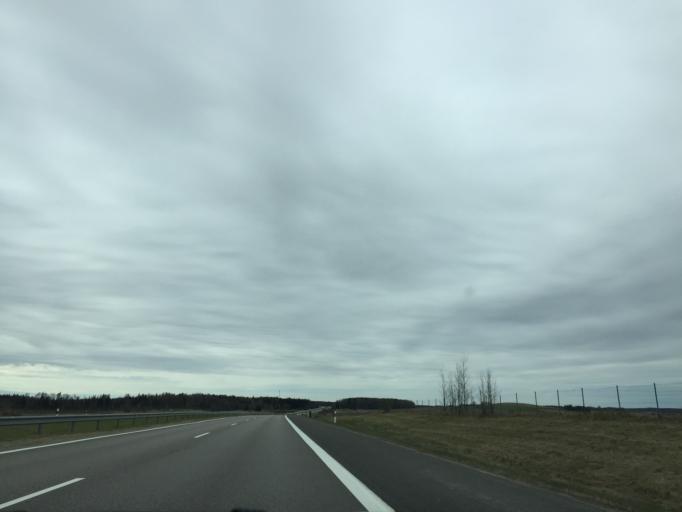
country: LT
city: Rietavas
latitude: 55.6720
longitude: 21.7222
